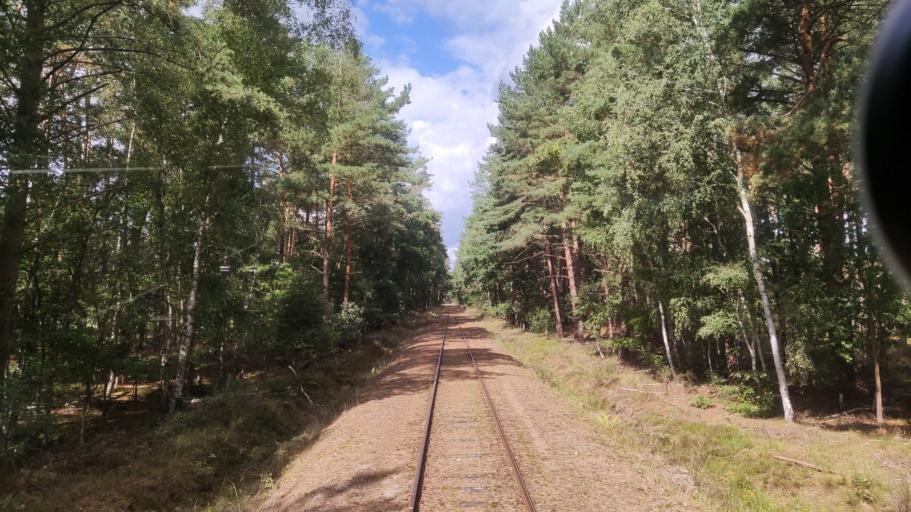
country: DE
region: Lower Saxony
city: Neetze
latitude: 53.2761
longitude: 10.6034
